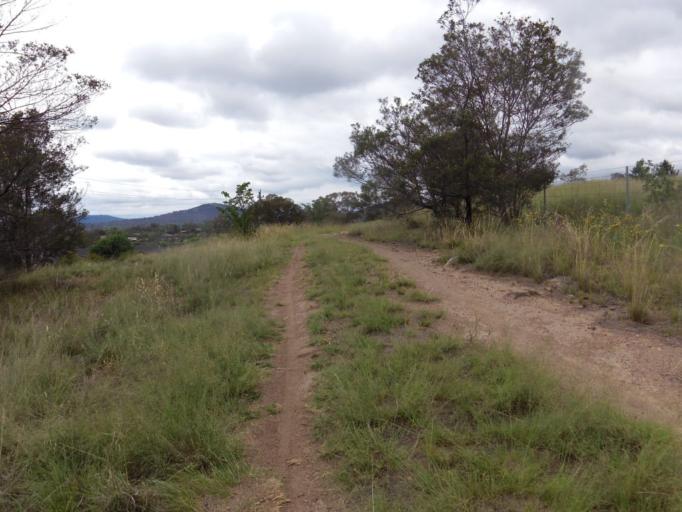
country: AU
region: Australian Capital Territory
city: Macquarie
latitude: -35.3392
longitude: 149.0274
